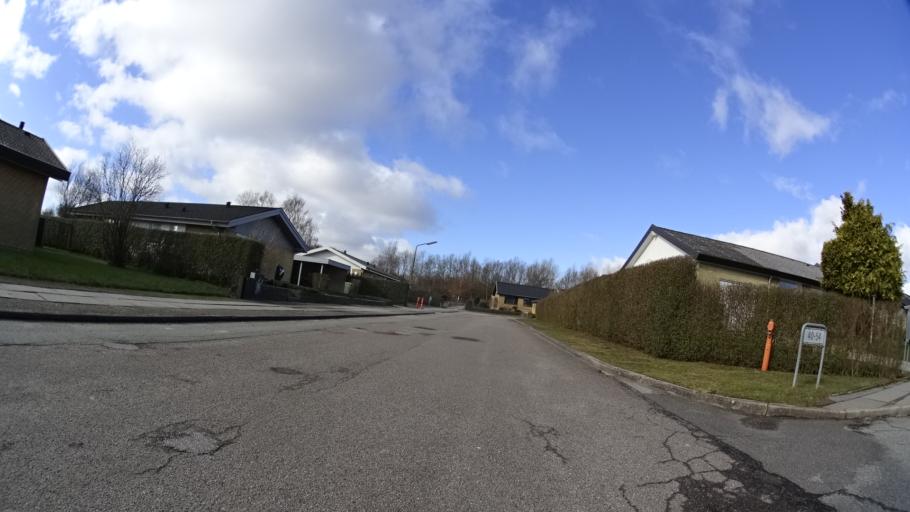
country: DK
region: Central Jutland
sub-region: Arhus Kommune
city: Tranbjerg
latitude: 56.0841
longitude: 10.1255
